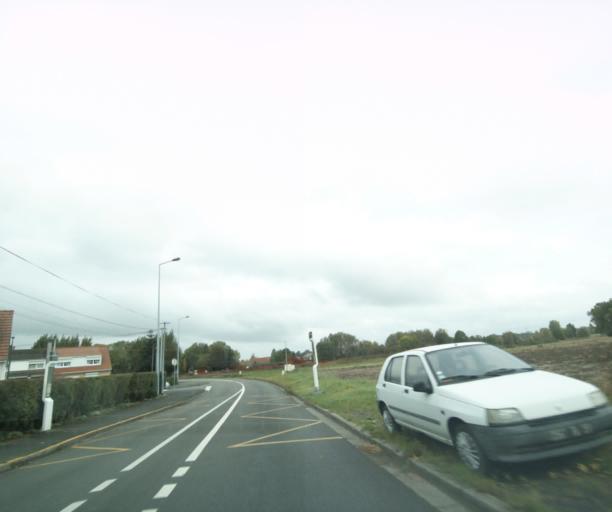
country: FR
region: Nord-Pas-de-Calais
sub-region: Departement du Nord
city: Roncq
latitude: 50.7591
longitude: 3.1126
